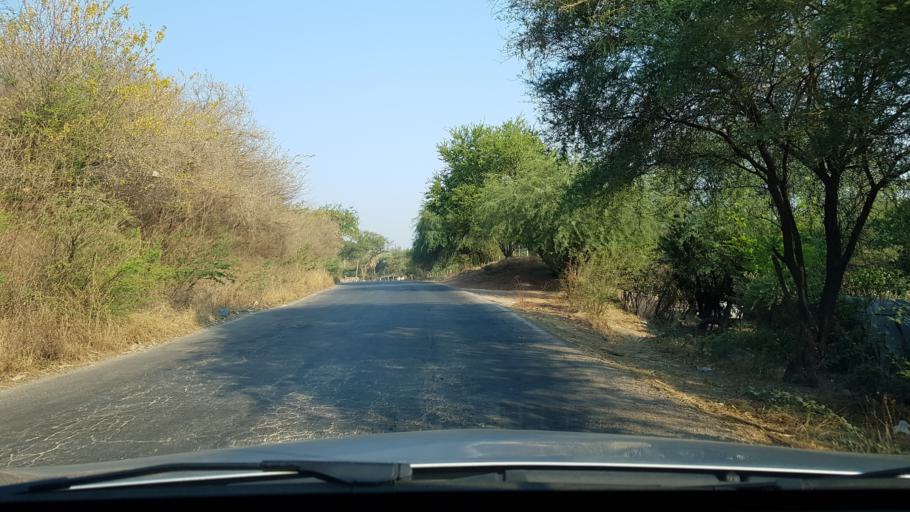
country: MX
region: Morelos
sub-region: Tepalcingo
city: Zacapalco
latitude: 18.6474
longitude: -99.0253
